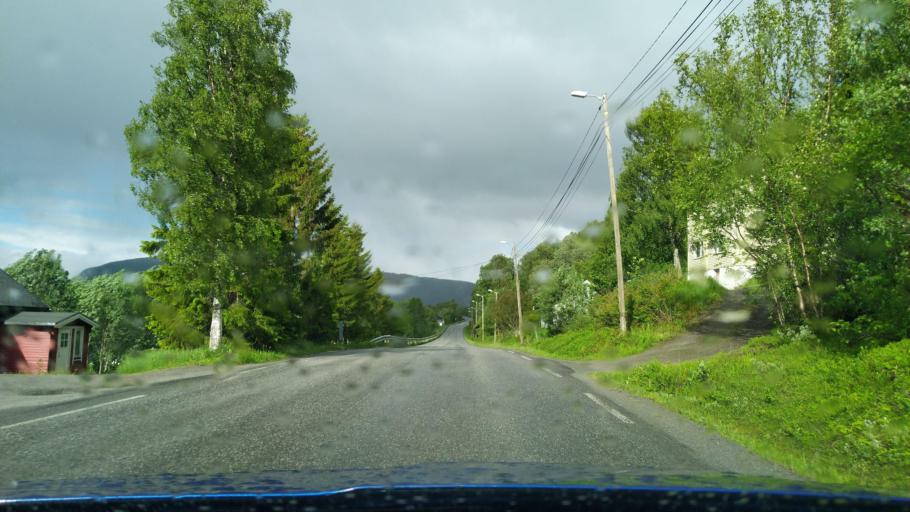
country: NO
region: Troms
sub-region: Sorreisa
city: Sorreisa
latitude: 69.1365
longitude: 18.0900
